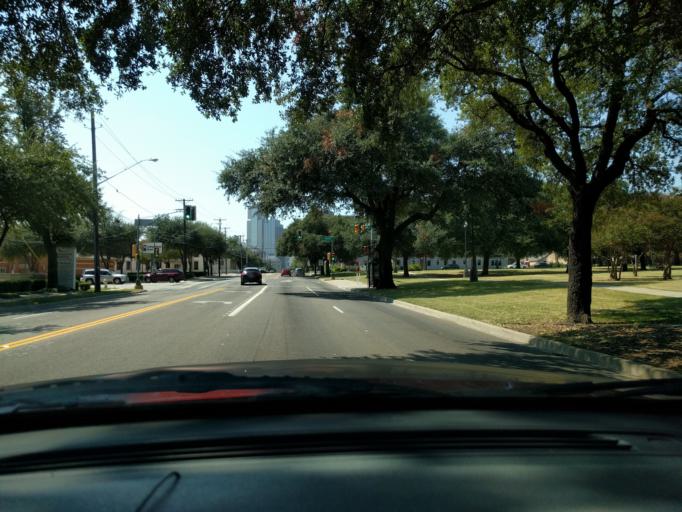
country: US
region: Texas
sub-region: Dallas County
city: Dallas
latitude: 32.7925
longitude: -96.7847
